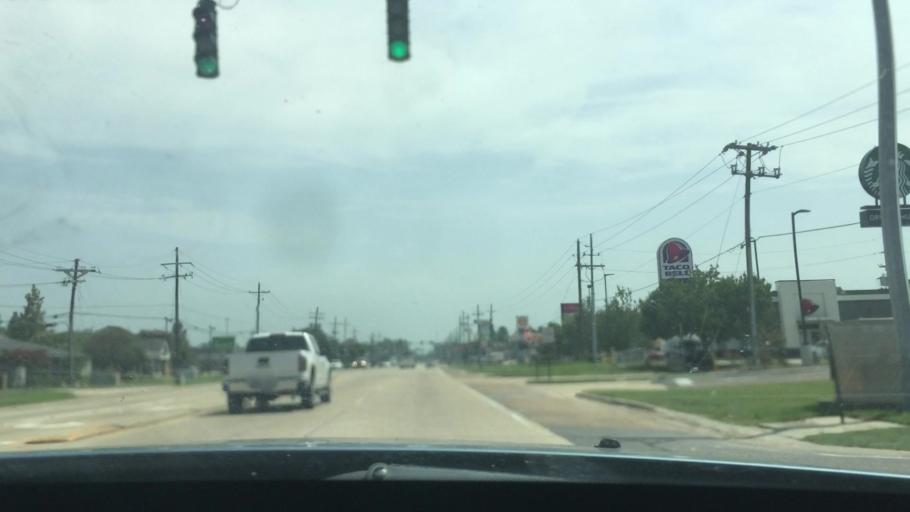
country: US
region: Louisiana
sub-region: East Baton Rouge Parish
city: Shenandoah
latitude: 30.4398
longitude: -91.0076
